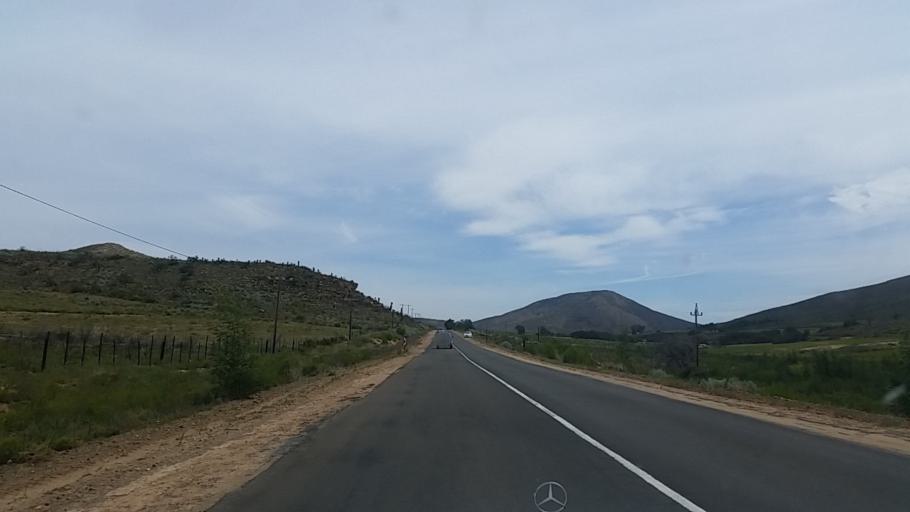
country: ZA
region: Western Cape
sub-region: Eden District Municipality
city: George
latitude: -33.8201
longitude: 22.3731
